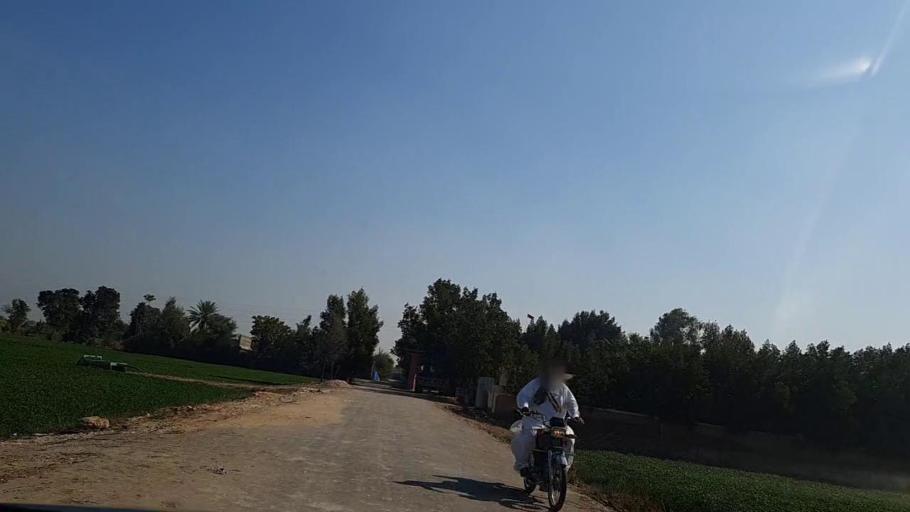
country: PK
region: Sindh
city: Sakrand
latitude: 26.2291
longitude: 68.3088
